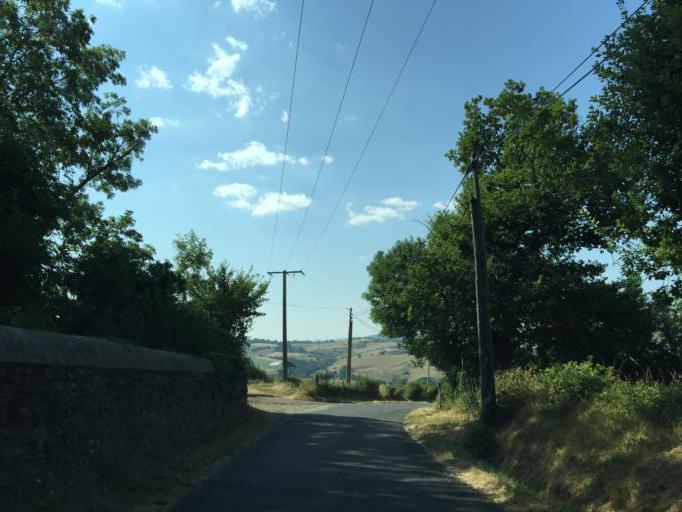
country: FR
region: Rhone-Alpes
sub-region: Departement de la Loire
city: Saint-Jean-Bonnefonds
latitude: 45.4469
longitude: 4.4910
